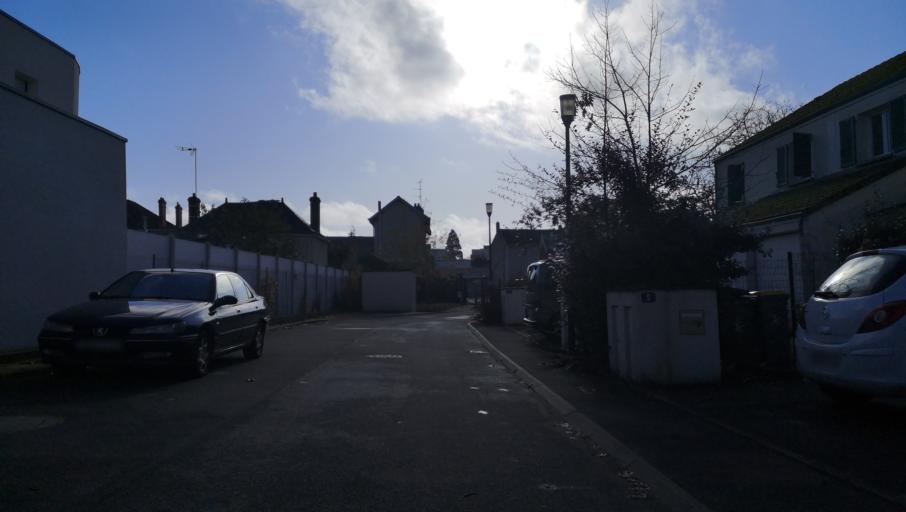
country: FR
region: Centre
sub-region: Departement du Loiret
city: Saint-Jean-le-Blanc
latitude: 47.9060
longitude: 1.9336
